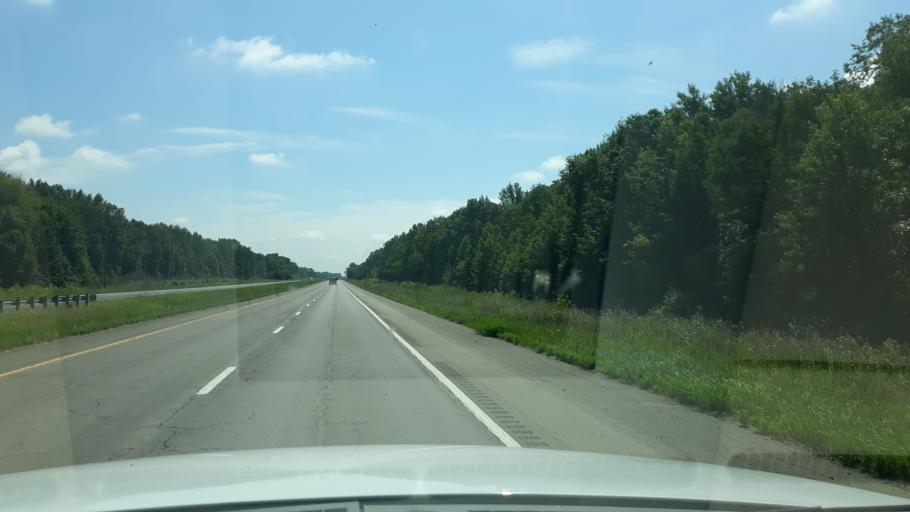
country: US
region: Illinois
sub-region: Saline County
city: Carrier Mills
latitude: 37.7333
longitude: -88.6683
